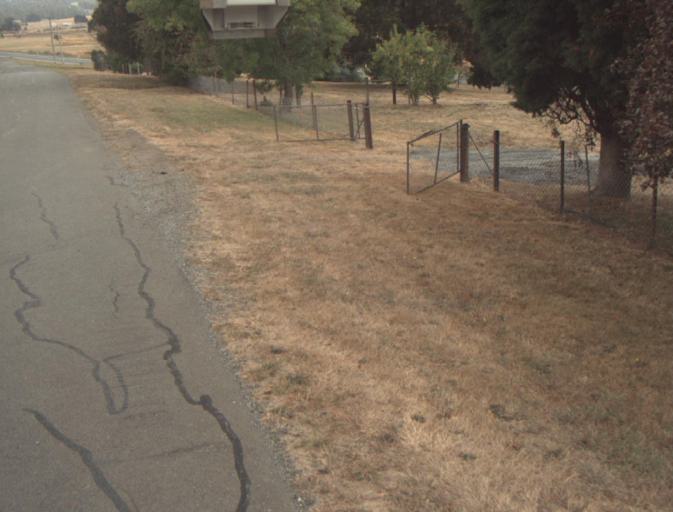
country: AU
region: Tasmania
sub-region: Launceston
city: Mayfield
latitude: -41.3270
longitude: 147.0656
